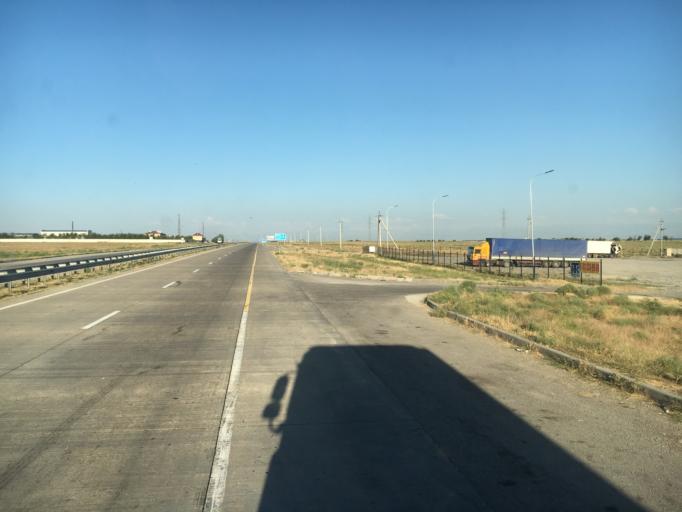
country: KZ
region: Ongtustik Qazaqstan
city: Shymkent
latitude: 42.4542
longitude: 69.6170
